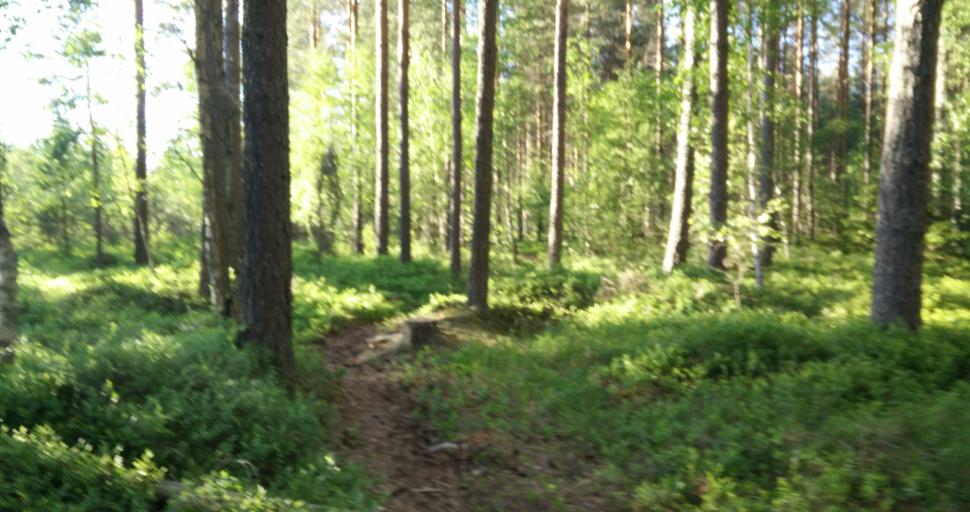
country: SE
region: Vaermland
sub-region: Hagfors Kommun
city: Hagfors
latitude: 60.0185
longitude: 13.5834
